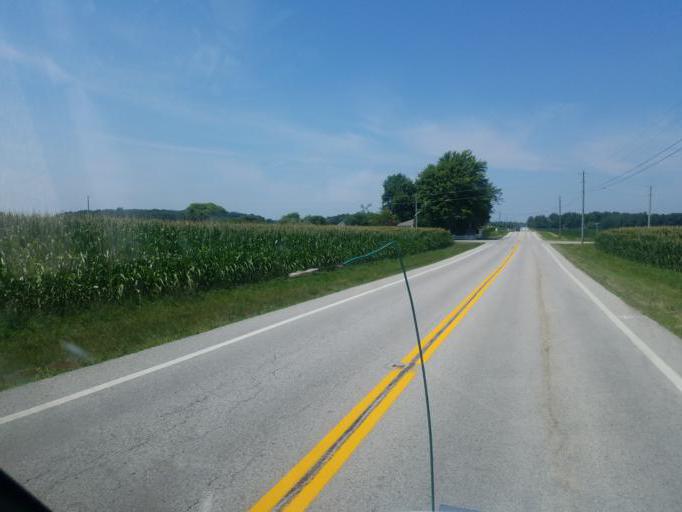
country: US
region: Ohio
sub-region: Auglaize County
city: New Bremen
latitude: 40.4796
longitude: -84.4345
